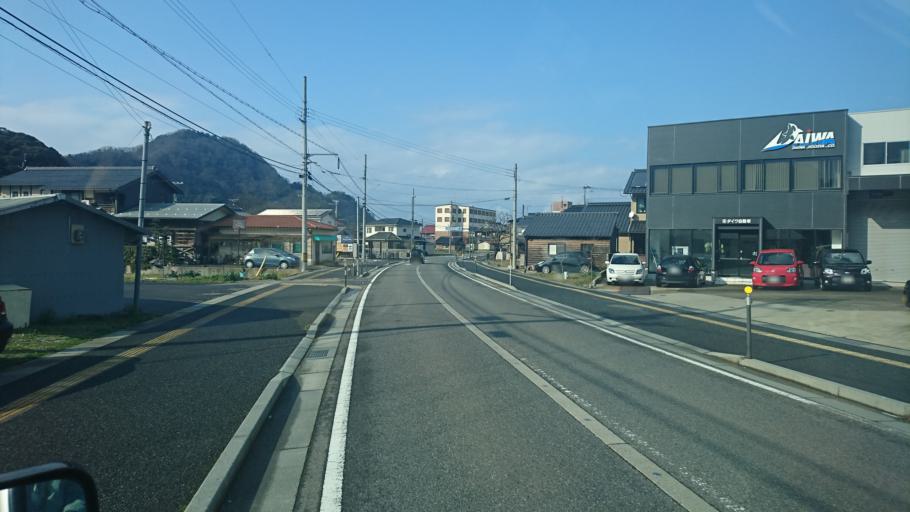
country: JP
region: Tottori
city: Tottori
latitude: 35.6242
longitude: 134.4456
